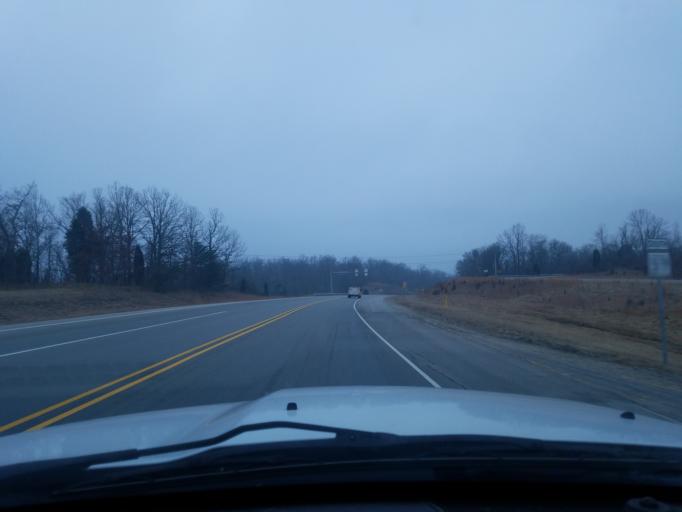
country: US
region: Indiana
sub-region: Perry County
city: Tell City
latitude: 38.0608
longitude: -86.6220
